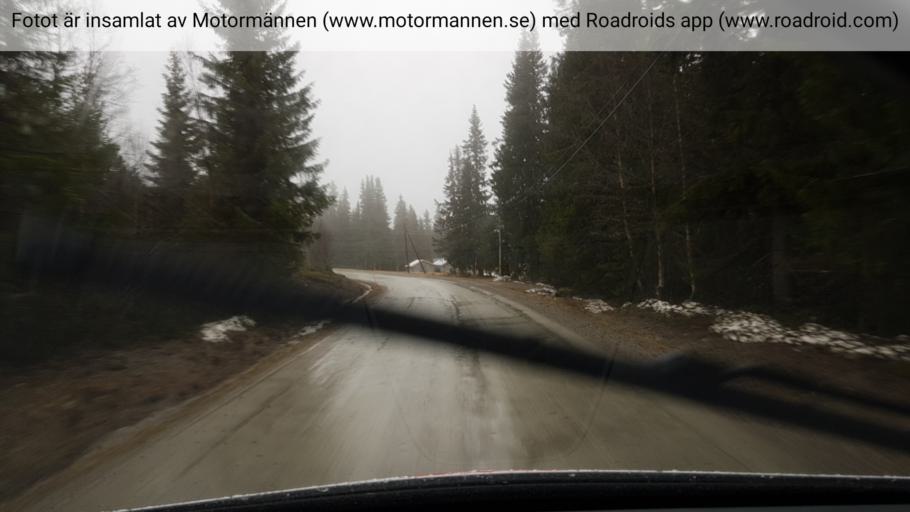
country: SE
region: Jaemtland
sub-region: Are Kommun
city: Jarpen
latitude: 62.5842
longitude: 13.3822
